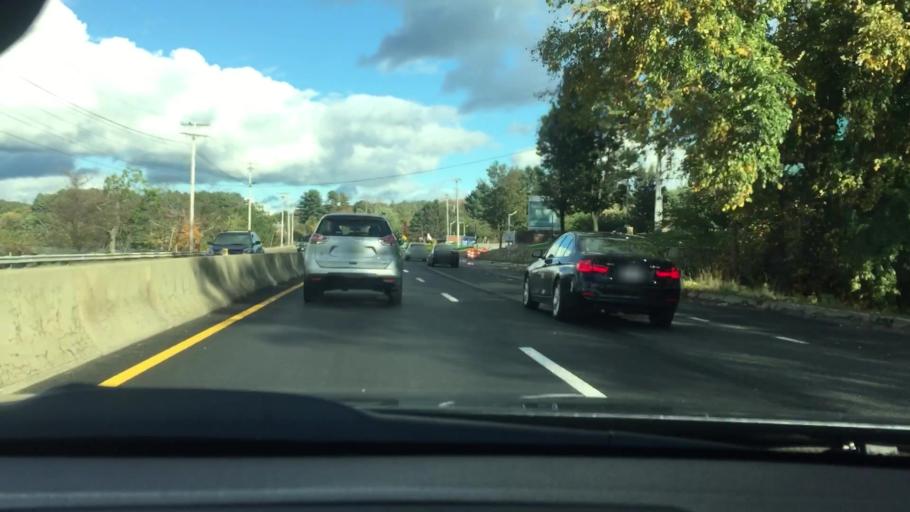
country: US
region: Massachusetts
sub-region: Worcester County
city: Southborough
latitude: 42.2927
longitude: -71.5174
